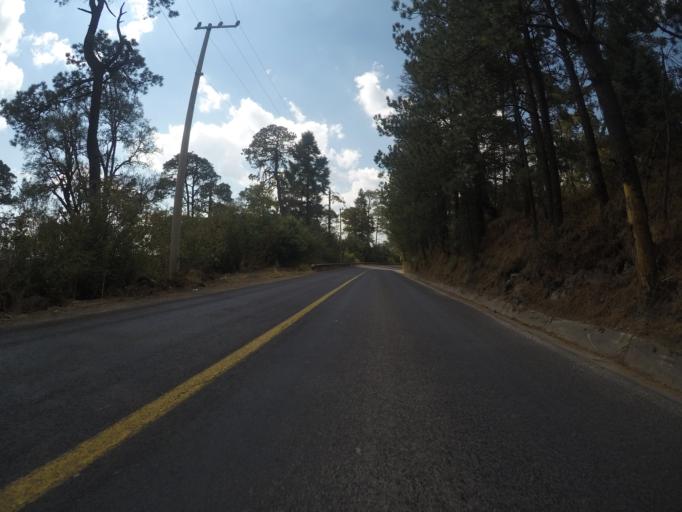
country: MX
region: Mexico
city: Cerro La Calera
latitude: 19.1551
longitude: -99.8051
